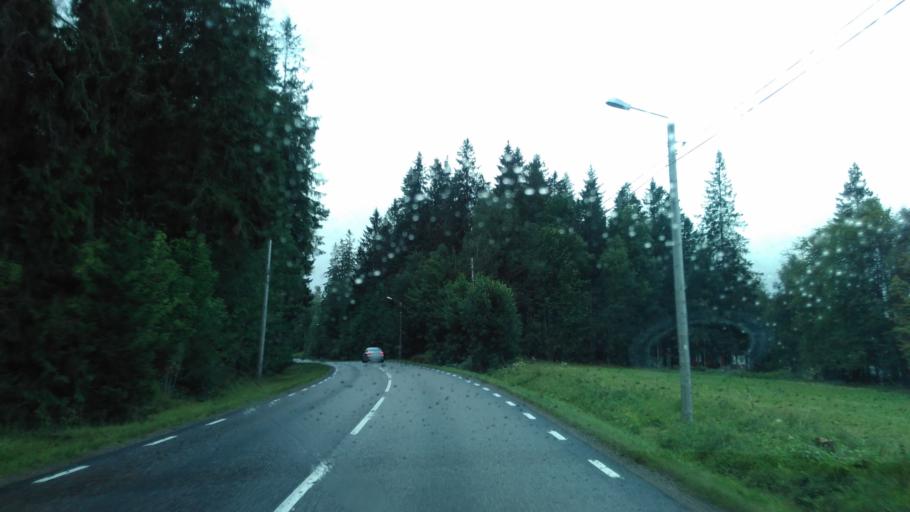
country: SE
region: Vaestra Goetaland
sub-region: Boras Kommun
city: Ganghester
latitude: 57.7622
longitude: 13.0182
